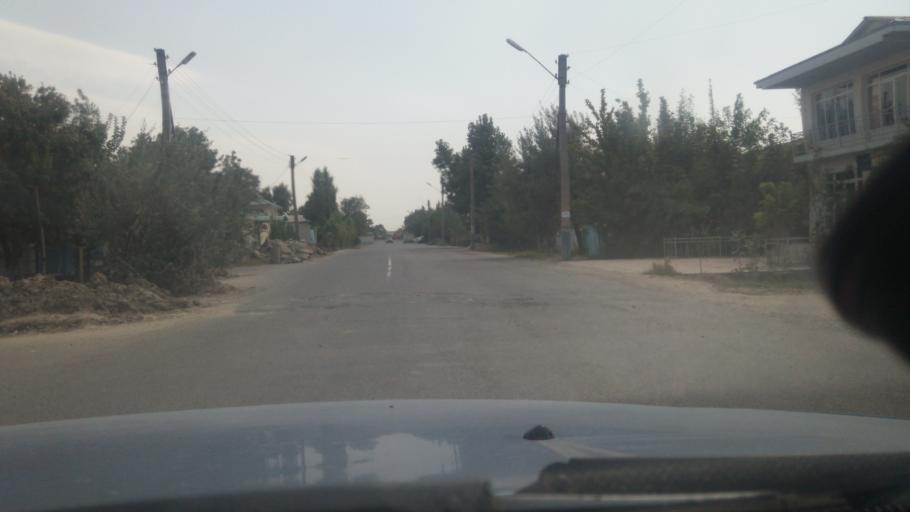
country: UZ
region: Sirdaryo
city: Guliston
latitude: 40.4948
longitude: 68.7828
